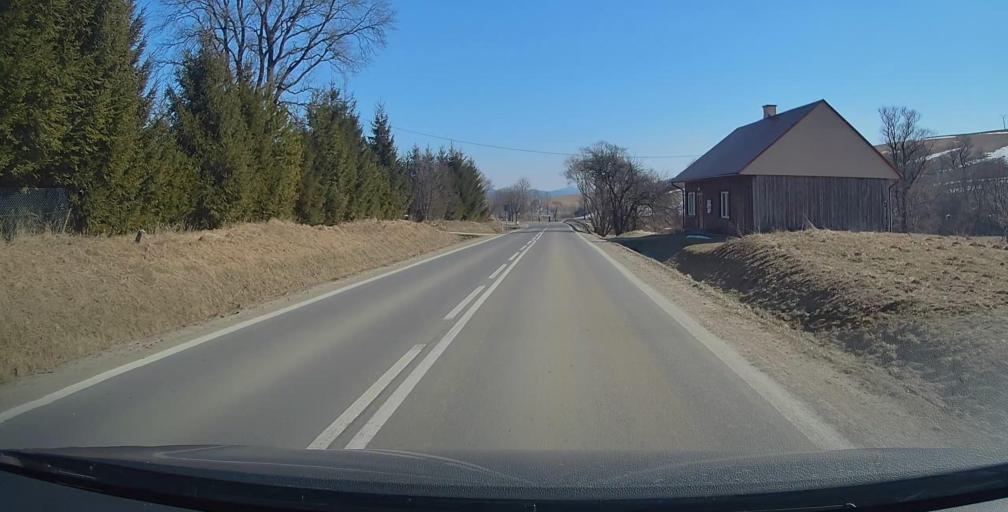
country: PL
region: Subcarpathian Voivodeship
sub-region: Powiat bieszczadzki
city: Ustrzyki Dolne
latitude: 49.5011
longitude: 22.6290
